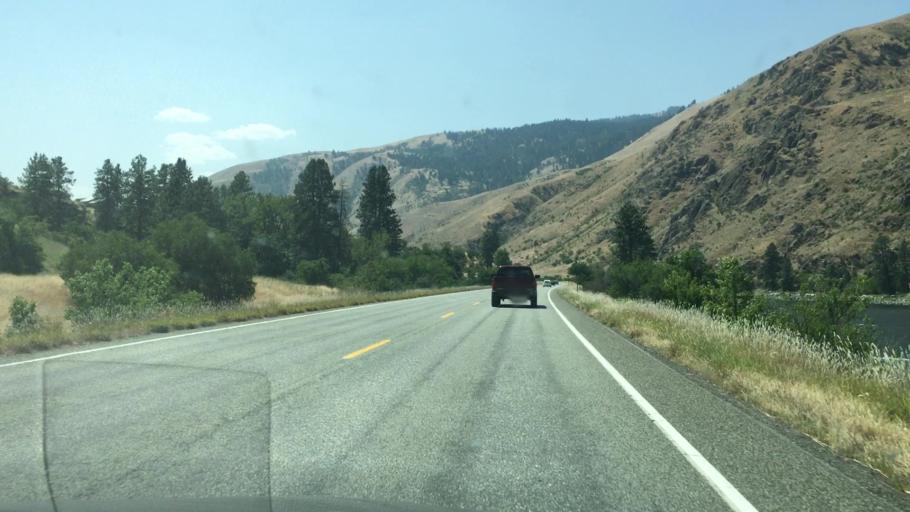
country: US
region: Idaho
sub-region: Idaho County
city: Grangeville
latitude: 45.5904
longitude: -116.2877
